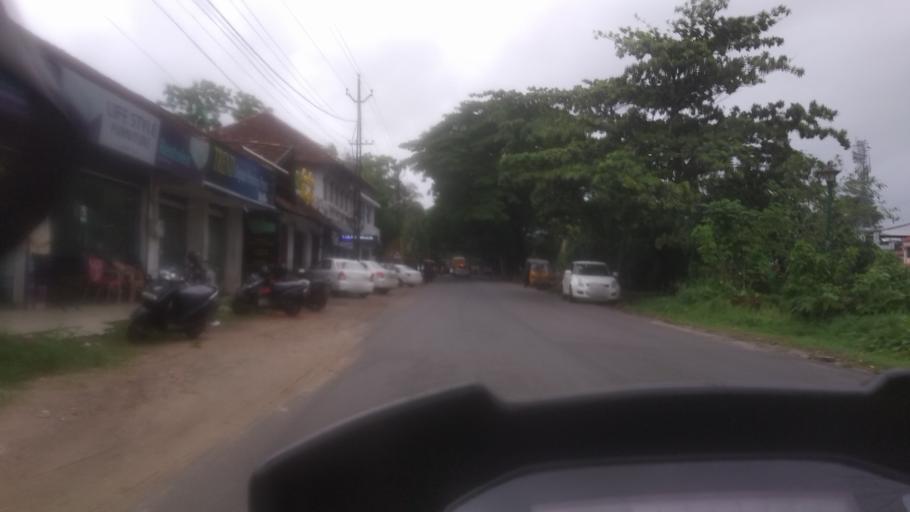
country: IN
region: Kerala
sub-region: Alappuzha
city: Alleppey
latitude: 9.4997
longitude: 76.3309
